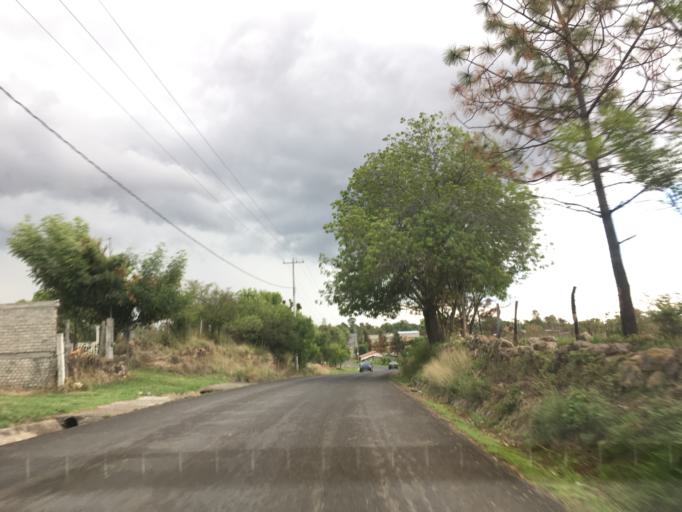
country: MX
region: Michoacan
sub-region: Morelia
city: La Mintzita (Piedra Dura)
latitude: 19.5852
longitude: -101.2737
